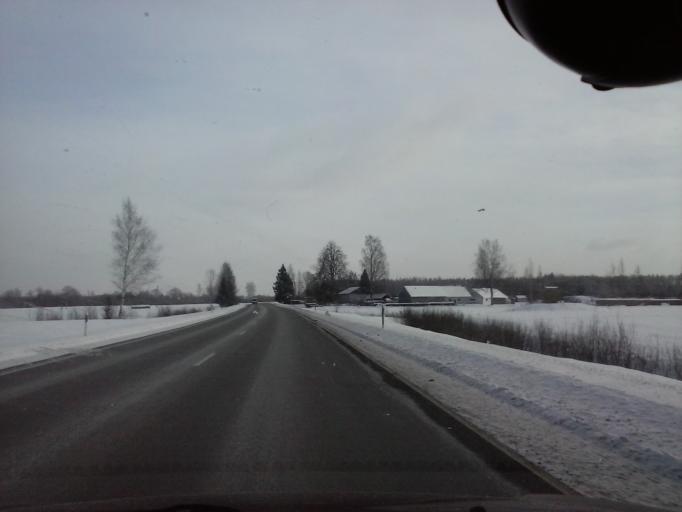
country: EE
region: Paernumaa
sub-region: Paikuse vald
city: Paikuse
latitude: 58.2021
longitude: 24.7290
